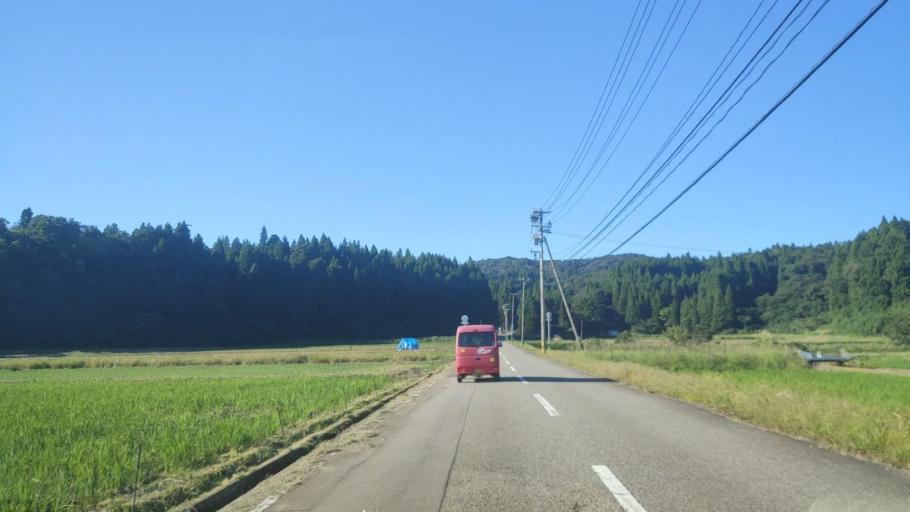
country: JP
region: Ishikawa
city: Nanao
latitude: 37.1057
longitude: 136.9622
